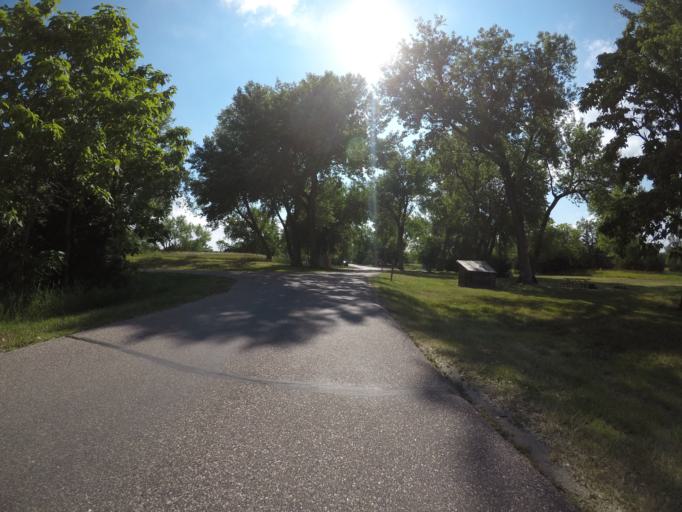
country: US
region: Nebraska
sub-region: Buffalo County
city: Kearney
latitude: 40.6547
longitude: -98.9933
